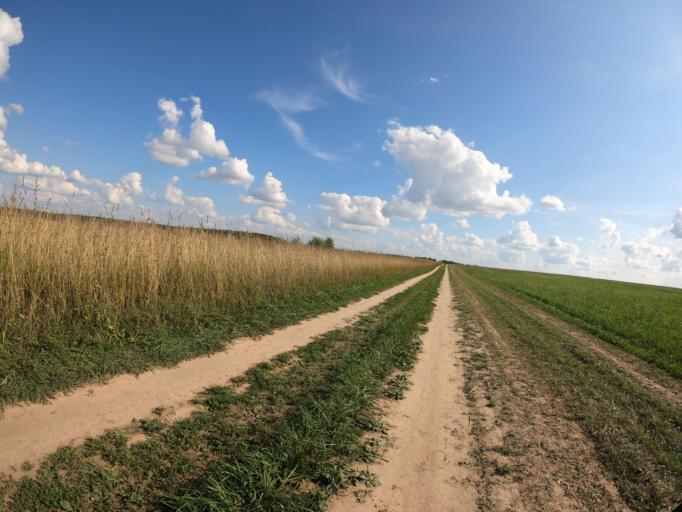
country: RU
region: Moskovskaya
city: Troitskoye
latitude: 55.2237
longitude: 38.4858
